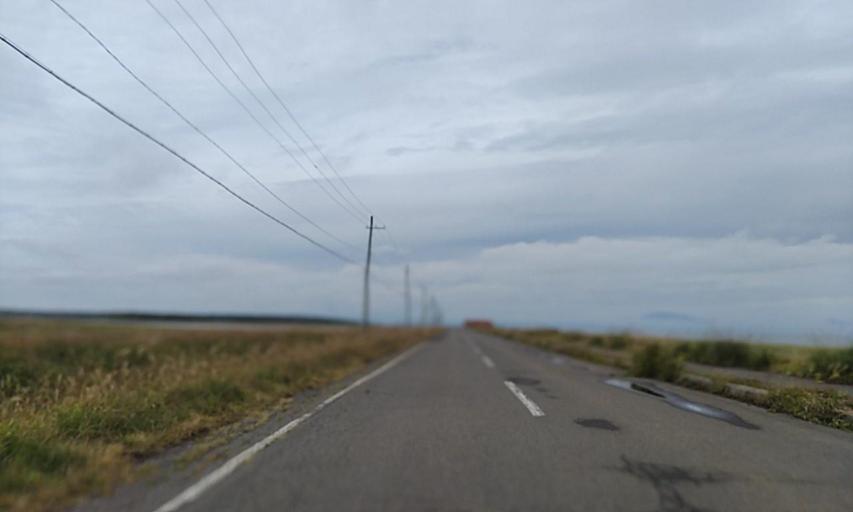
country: JP
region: Hokkaido
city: Shibetsu
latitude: 43.6015
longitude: 145.3076
